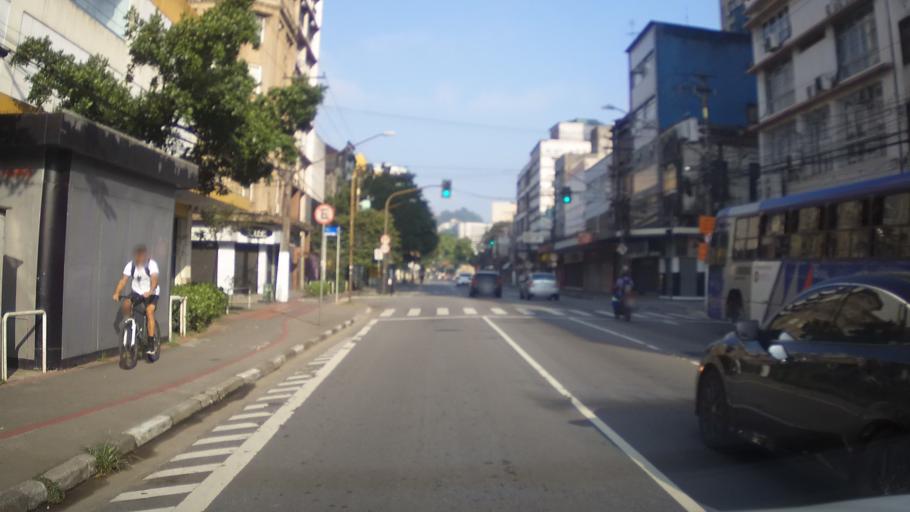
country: BR
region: Sao Paulo
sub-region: Santos
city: Santos
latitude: -23.9348
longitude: -46.3282
